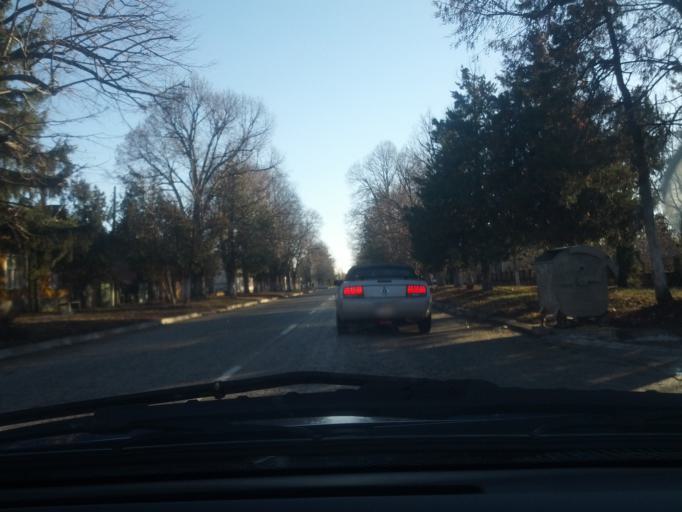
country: BG
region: Vratsa
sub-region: Obshtina Miziya
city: Miziya
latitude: 43.5946
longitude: 23.8186
